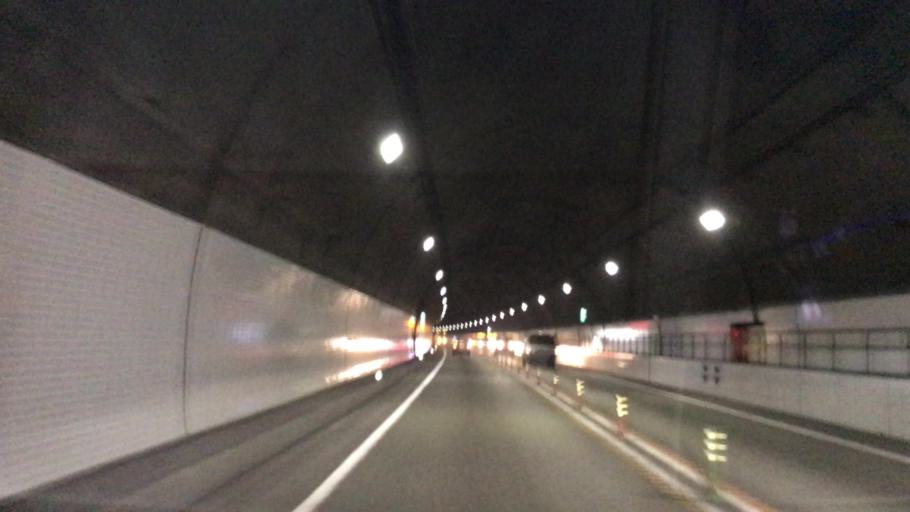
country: JP
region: Hokkaido
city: Iwamizawa
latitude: 42.9291
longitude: 142.1230
